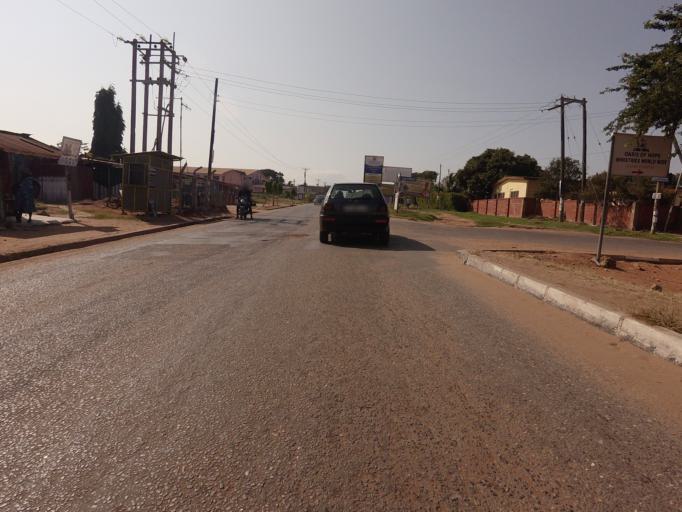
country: GH
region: Greater Accra
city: Teshi Old Town
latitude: 5.5903
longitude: -0.0994
